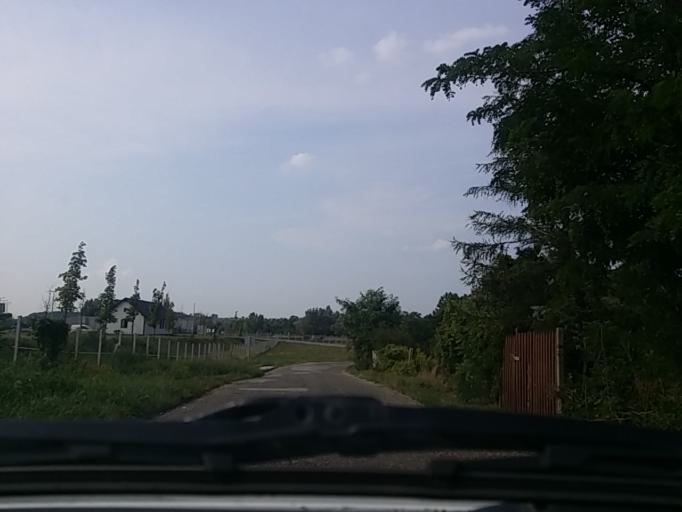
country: HU
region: Komarom-Esztergom
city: Tatabanya
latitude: 47.5339
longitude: 18.4316
